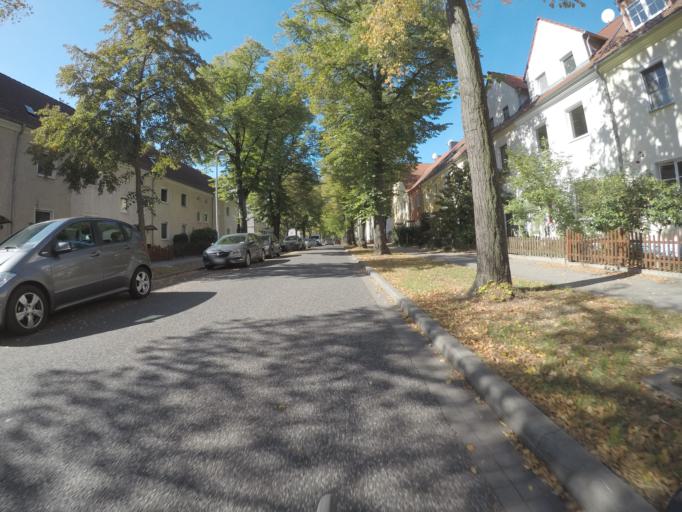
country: DE
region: Brandenburg
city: Hennigsdorf
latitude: 52.6418
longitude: 13.1981
